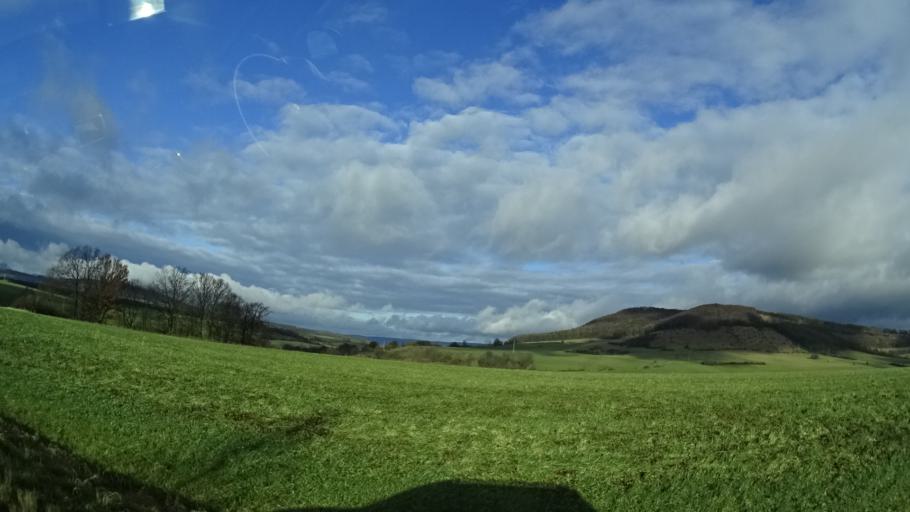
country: DE
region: Thuringia
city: Wiesenthal
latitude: 50.7029
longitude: 10.1754
